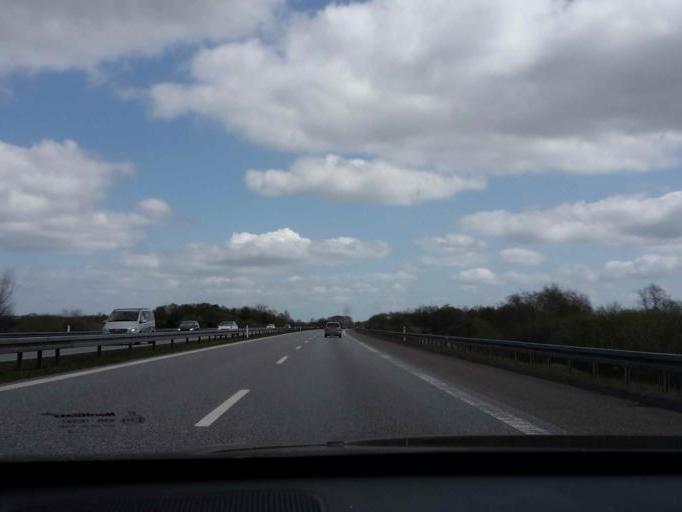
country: DK
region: South Denmark
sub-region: Esbjerg Kommune
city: Bramming
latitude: 55.5129
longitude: 8.7543
